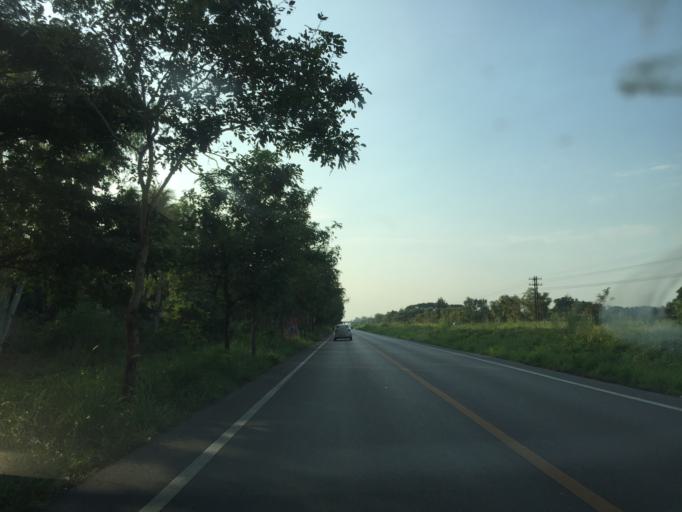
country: TH
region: Chiang Mai
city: Saraphi
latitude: 18.7425
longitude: 99.0281
